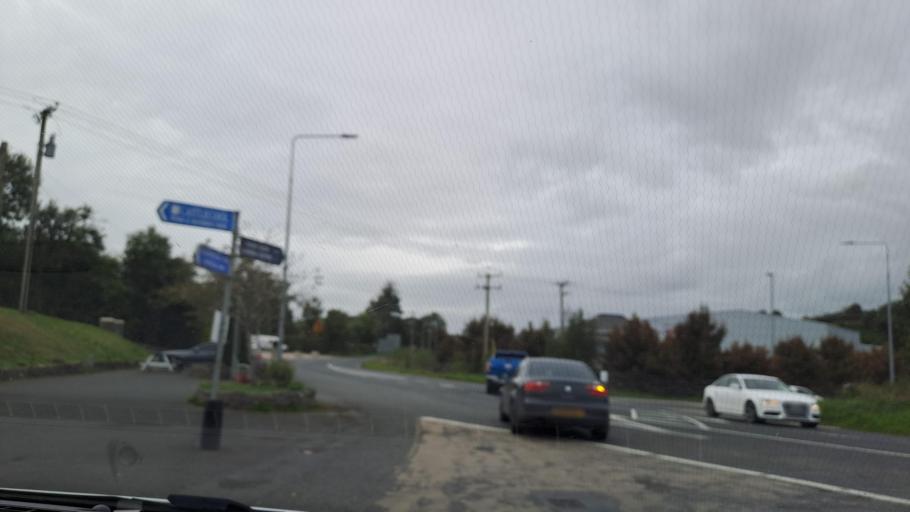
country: IE
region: Ulster
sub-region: County Monaghan
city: Castleblayney
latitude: 54.0651
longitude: -6.8128
